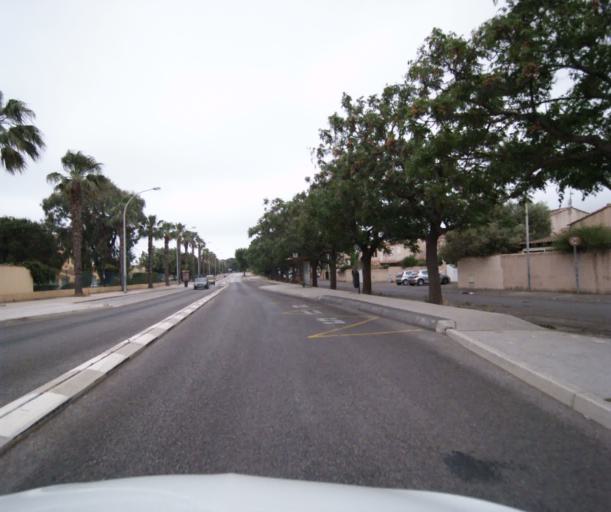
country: FR
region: Provence-Alpes-Cote d'Azur
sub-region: Departement du Var
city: La Seyne-sur-Mer
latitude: 43.0874
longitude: 5.8908
